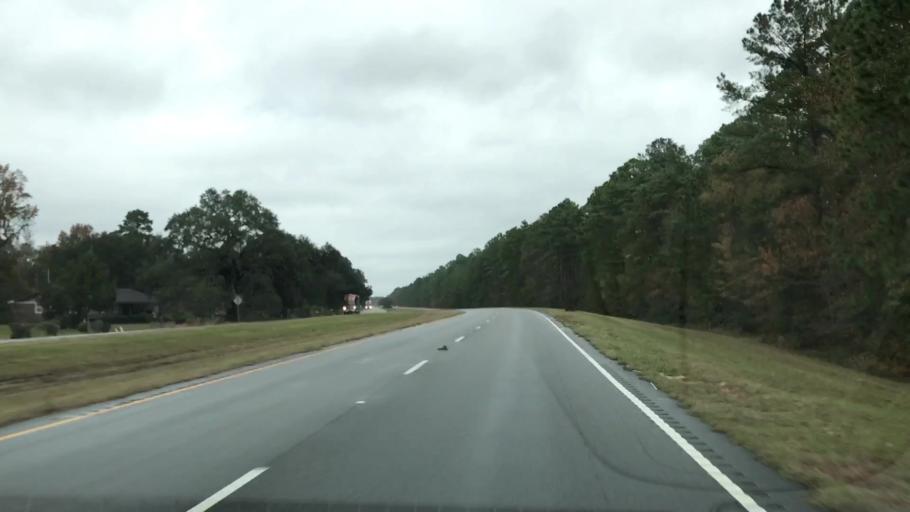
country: US
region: South Carolina
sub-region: Georgetown County
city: Georgetown
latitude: 33.2306
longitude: -79.3763
